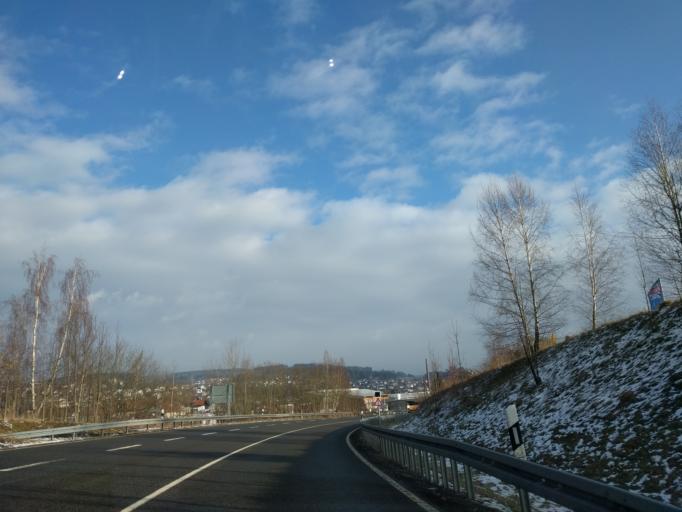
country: DE
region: Bavaria
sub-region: Lower Bavaria
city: Regen
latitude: 48.9661
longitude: 13.1326
